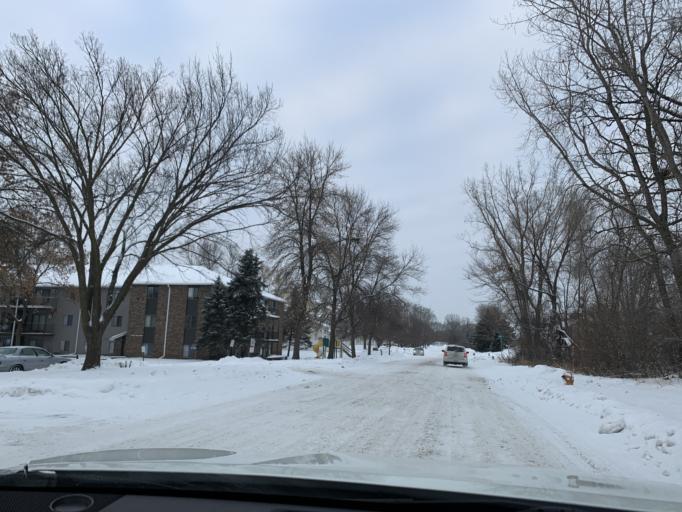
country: US
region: Minnesota
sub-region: Anoka County
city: Coon Rapids
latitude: 45.1636
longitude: -93.2920
